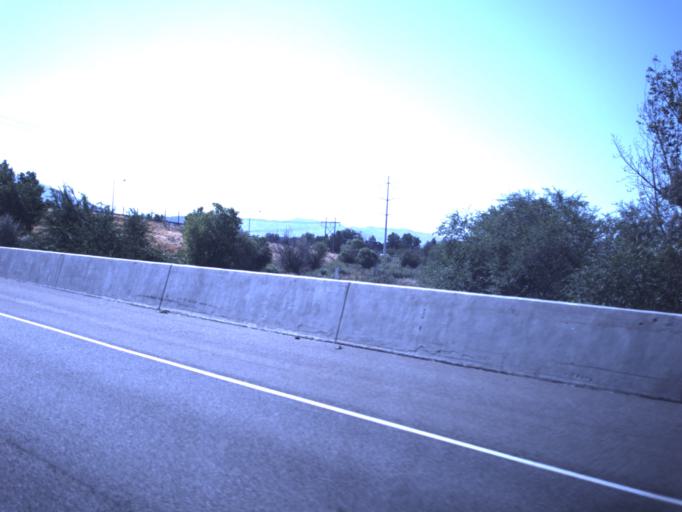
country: US
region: Utah
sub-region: Salt Lake County
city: West Jordan
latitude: 40.6386
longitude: -111.9220
